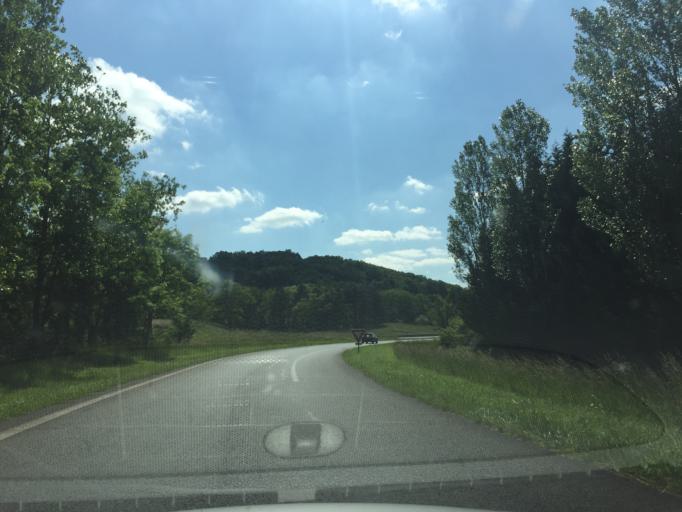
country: FR
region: Aquitaine
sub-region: Departement du Lot-et-Garonne
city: Boe
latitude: 44.1632
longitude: 0.6042
